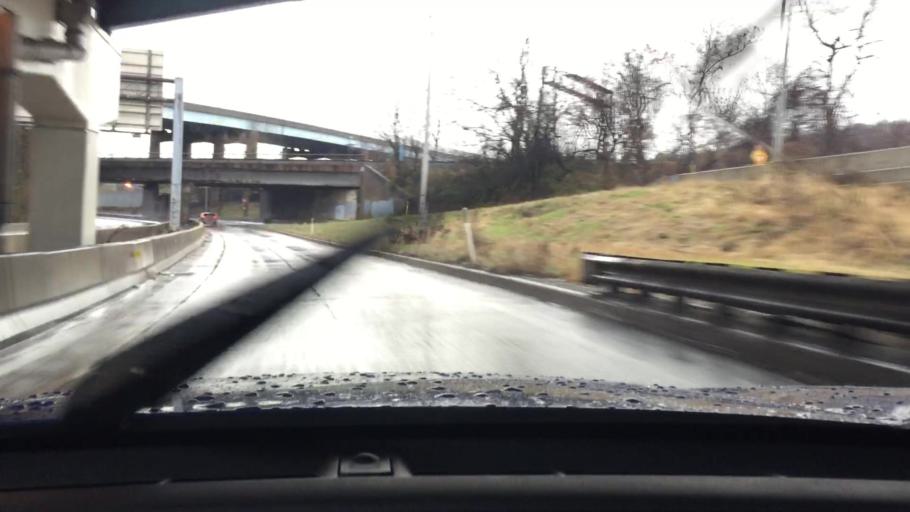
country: US
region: Pennsylvania
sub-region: Allegheny County
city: West Homestead
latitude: 40.3929
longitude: -79.9337
